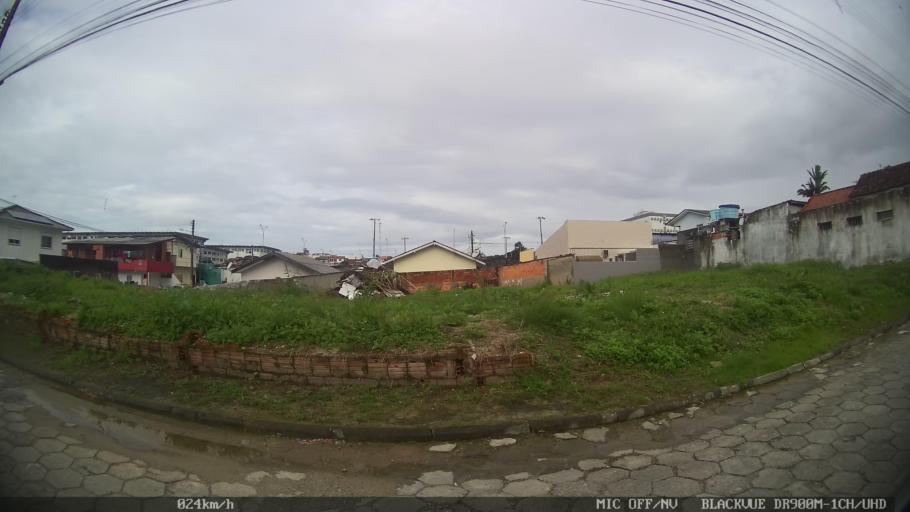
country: BR
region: Santa Catarina
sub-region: Sao Jose
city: Campinas
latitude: -27.5506
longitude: -48.6326
